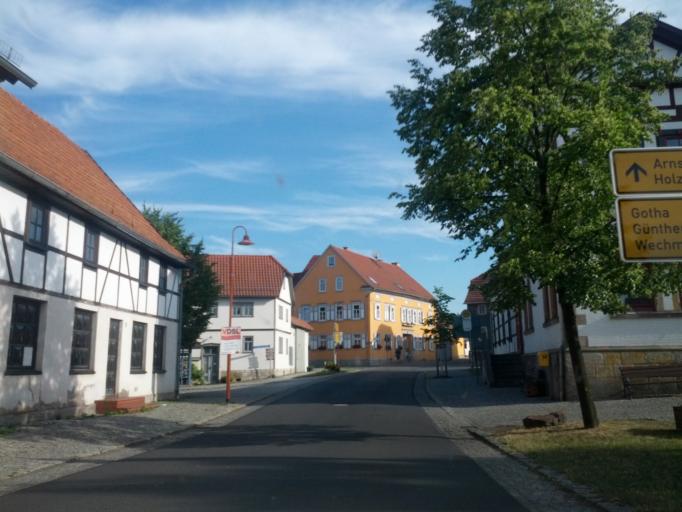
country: DE
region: Thuringia
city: Wandersleben
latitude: 50.8681
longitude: 10.8248
